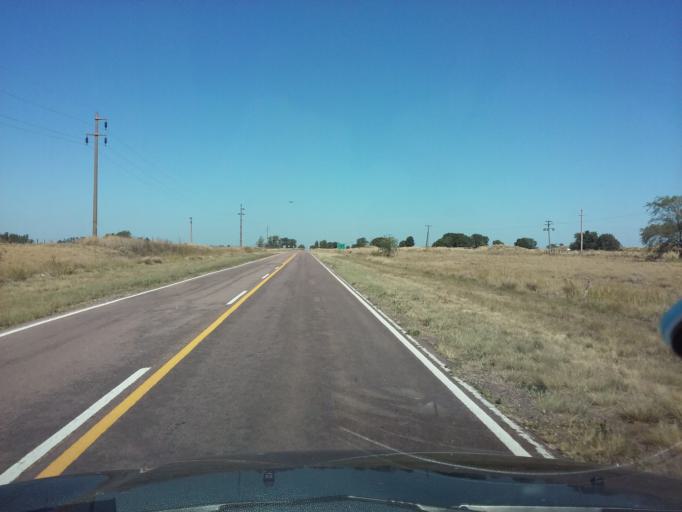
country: AR
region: La Pampa
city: Uriburu
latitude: -36.4138
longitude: -63.9431
